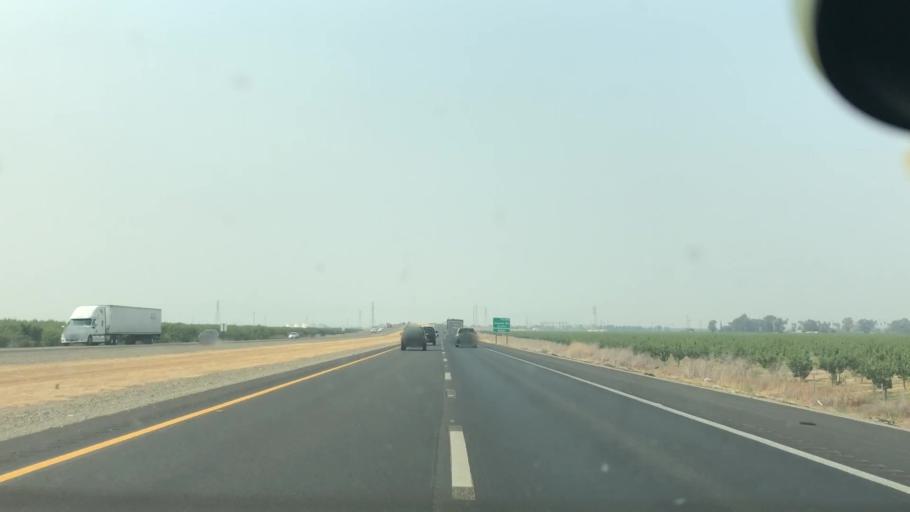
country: US
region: California
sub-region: San Joaquin County
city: Tracy
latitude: 37.7344
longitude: -121.3434
